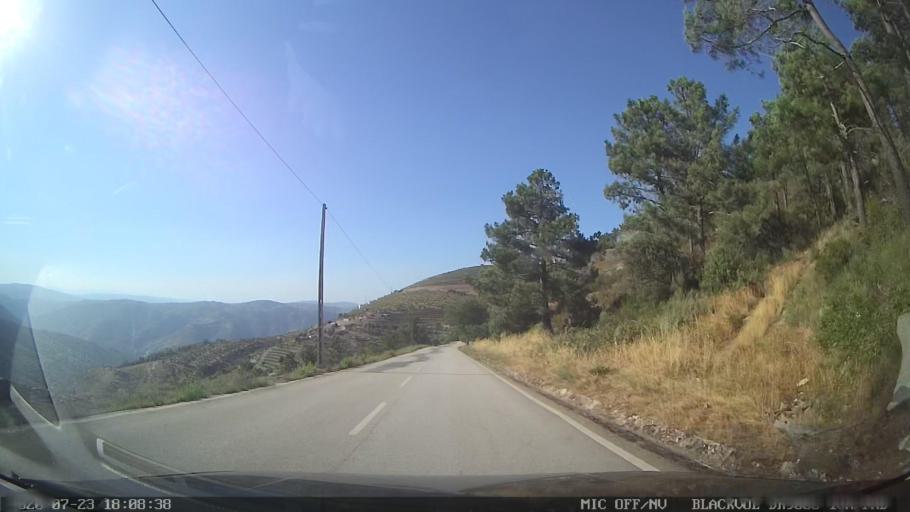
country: PT
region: Viseu
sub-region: Sao Joao da Pesqueira
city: Sao Joao da Pesqueira
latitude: 41.1769
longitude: -7.4371
